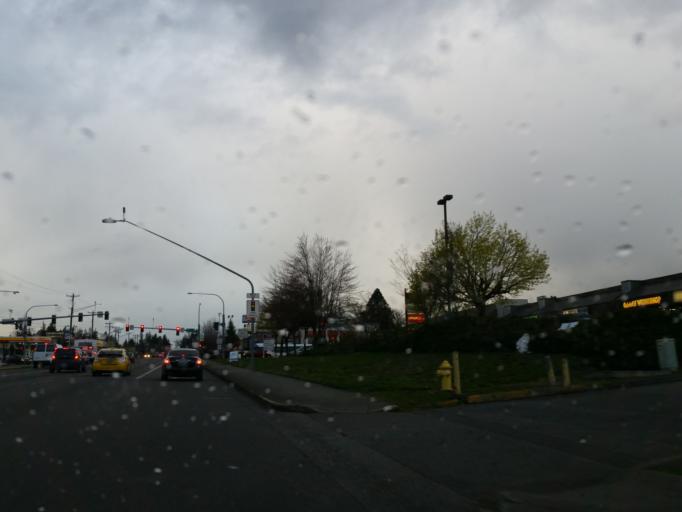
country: US
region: Washington
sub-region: Snohomish County
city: Alderwood Manor
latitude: 47.8162
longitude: -122.2922
